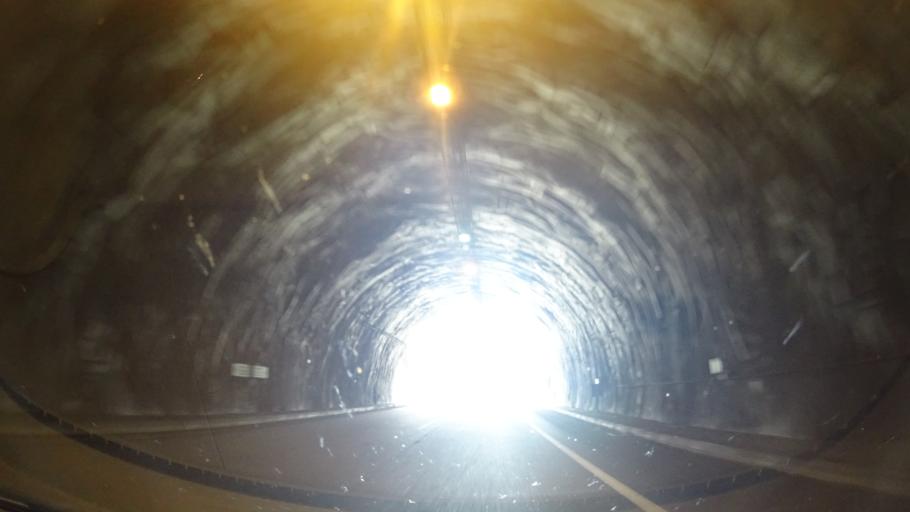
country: ES
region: Asturias
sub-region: Province of Asturias
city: Sama
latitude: 43.3430
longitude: -5.7016
